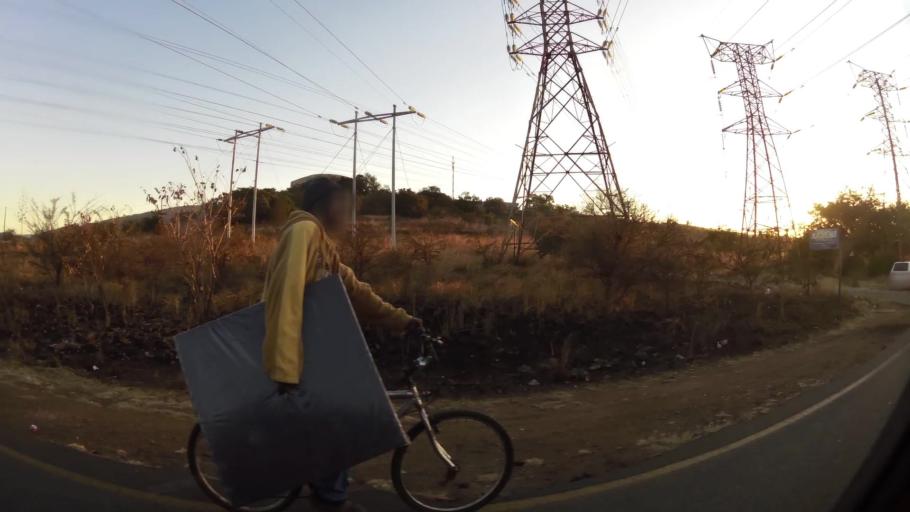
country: ZA
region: North-West
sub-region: Bojanala Platinum District Municipality
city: Rustenburg
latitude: -25.6313
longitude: 27.2020
